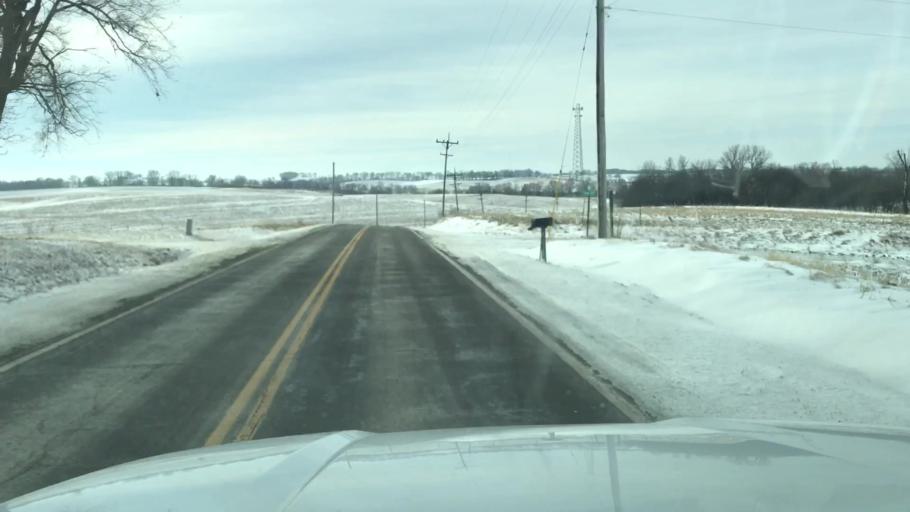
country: US
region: Missouri
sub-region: Holt County
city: Oregon
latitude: 40.0507
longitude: -95.1358
